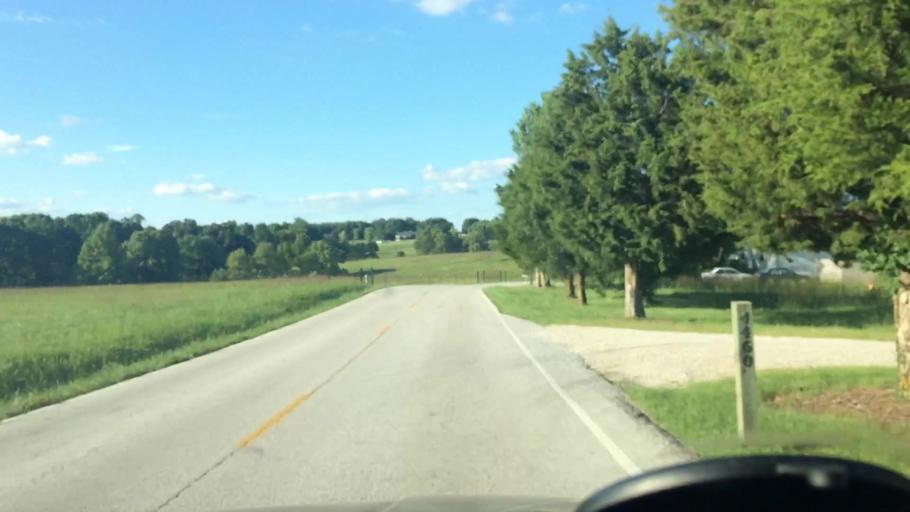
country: US
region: Missouri
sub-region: Greene County
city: Strafford
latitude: 37.2731
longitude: -93.0813
